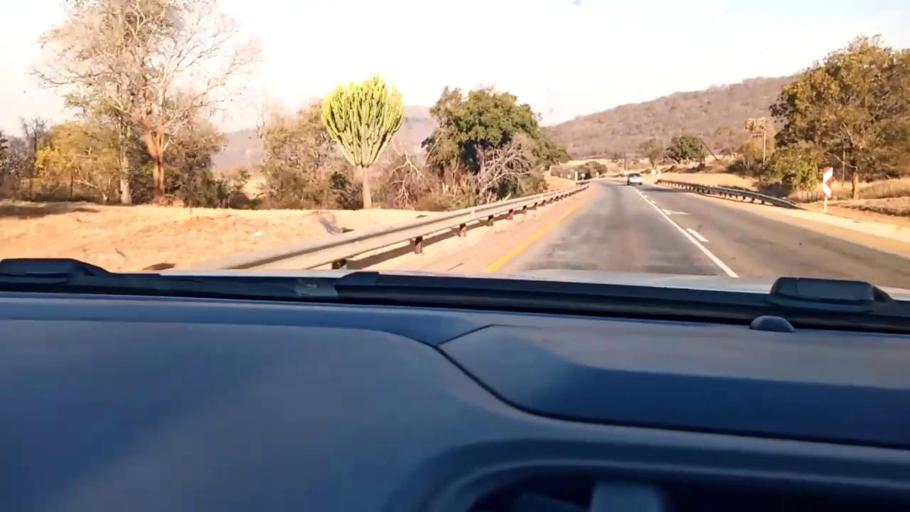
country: ZA
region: Limpopo
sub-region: Mopani District Municipality
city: Duiwelskloof
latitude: -23.6422
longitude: 30.1601
